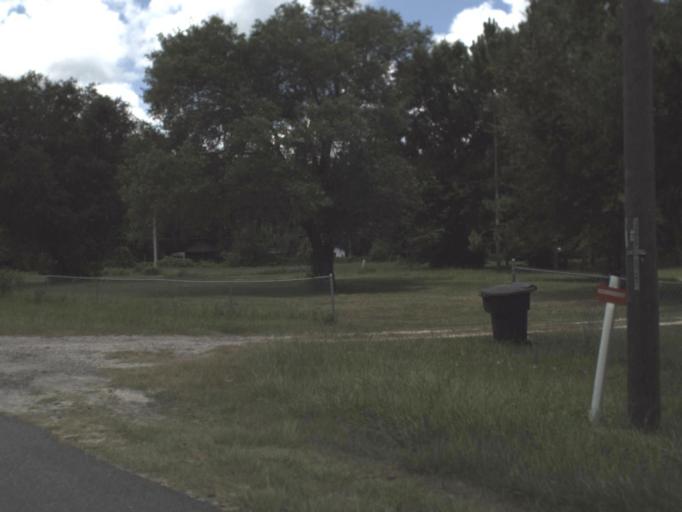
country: US
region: Florida
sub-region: Taylor County
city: Perry
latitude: 30.1077
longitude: -83.6008
